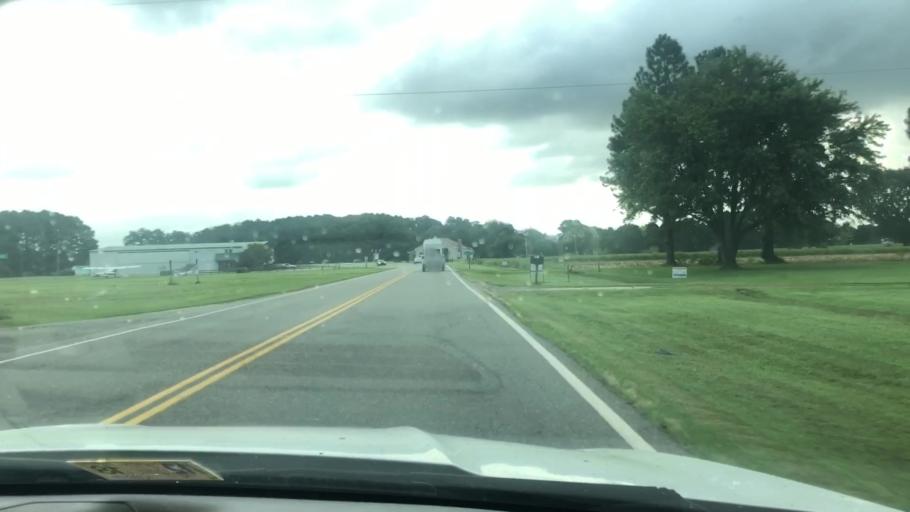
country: US
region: Virginia
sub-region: Middlesex County
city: Deltaville
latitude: 37.5981
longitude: -76.4480
